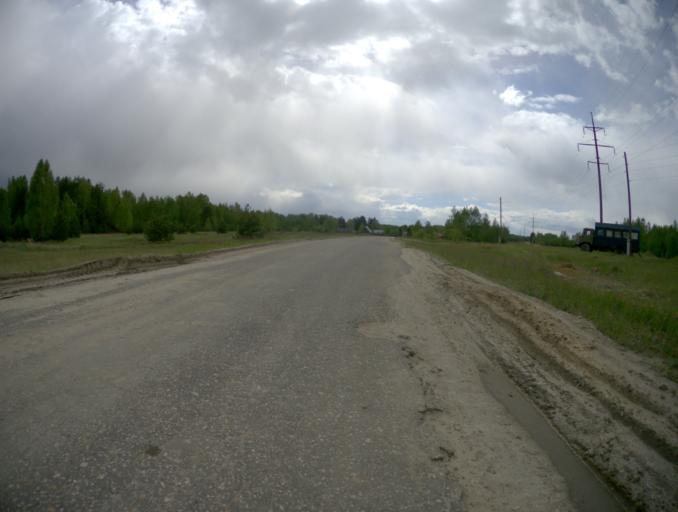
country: RU
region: Vladimir
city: Velikodvorskiy
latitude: 55.2285
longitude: 40.6471
